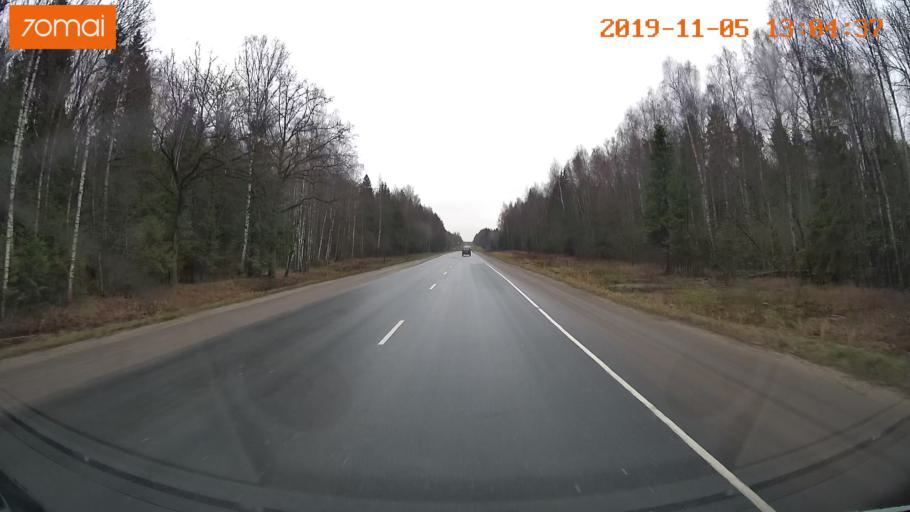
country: RU
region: Ivanovo
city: Kitovo
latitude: 56.8879
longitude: 41.2251
